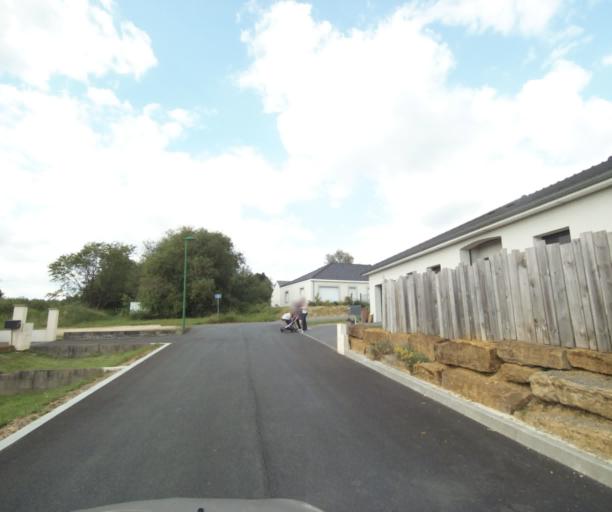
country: FR
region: Champagne-Ardenne
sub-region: Departement des Ardennes
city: Montcy-Notre-Dame
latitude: 49.7626
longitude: 4.7373
